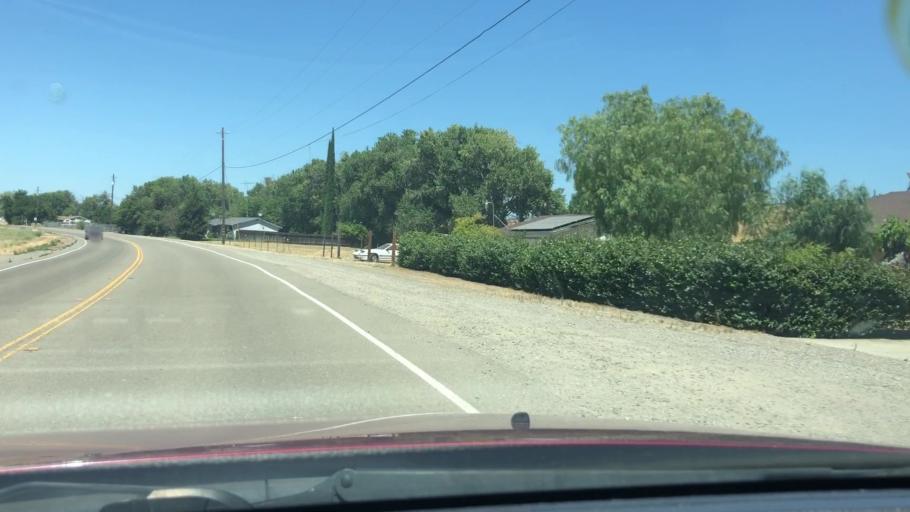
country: US
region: California
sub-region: San Joaquin County
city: Lathrop
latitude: 37.7908
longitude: -121.3024
